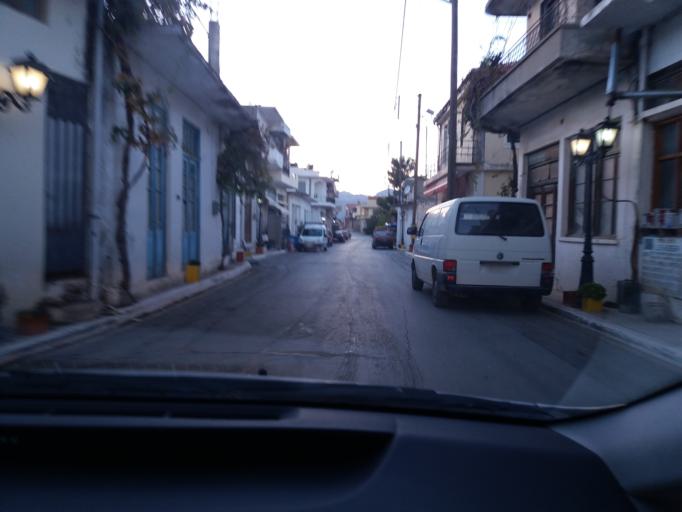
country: GR
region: Crete
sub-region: Nomos Irakleiou
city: Mokhos
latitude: 35.1663
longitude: 25.4838
